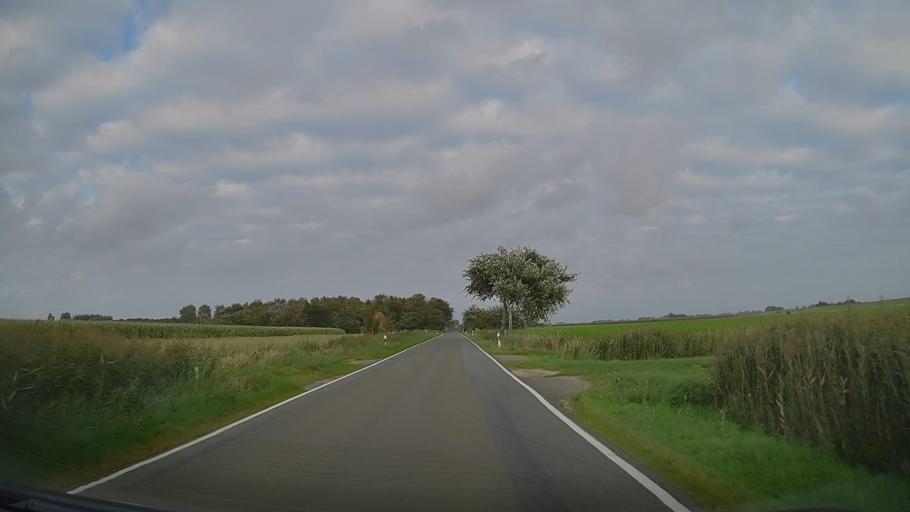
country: DE
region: Schleswig-Holstein
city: Osterhever
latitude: 54.4014
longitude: 8.7794
